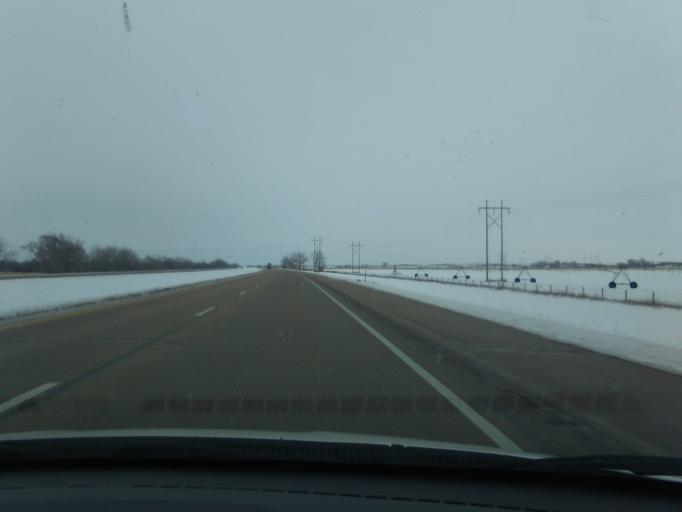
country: US
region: Nebraska
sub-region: Keith County
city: Ogallala
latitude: 41.0958
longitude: -101.8056
